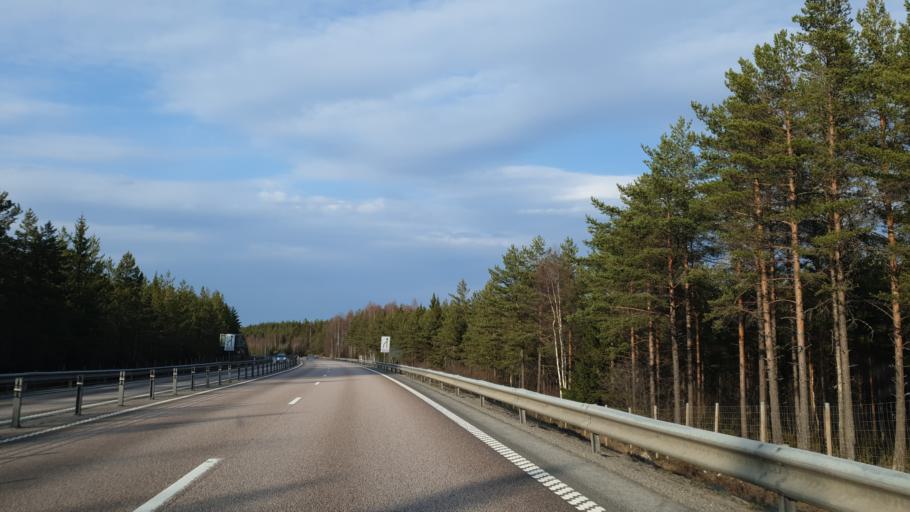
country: SE
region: Gaevleborg
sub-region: Hudiksvalls Kommun
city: Hudiksvall
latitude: 61.7805
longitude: 17.1303
